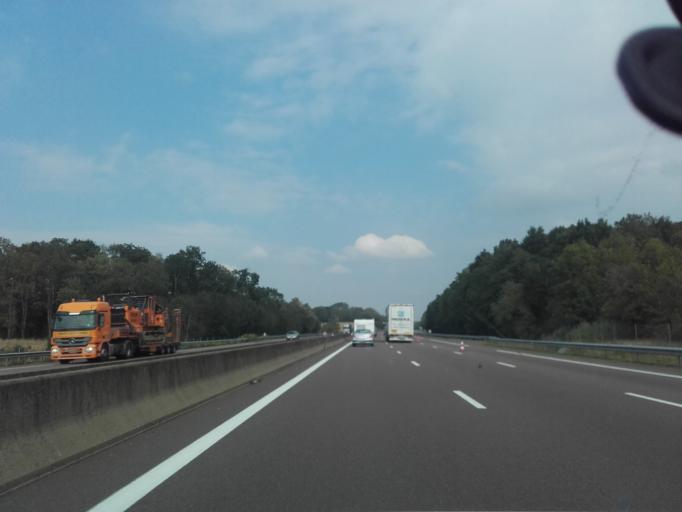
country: FR
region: Bourgogne
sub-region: Departement de Saone-et-Loire
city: Tournus
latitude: 46.5178
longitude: 4.9135
